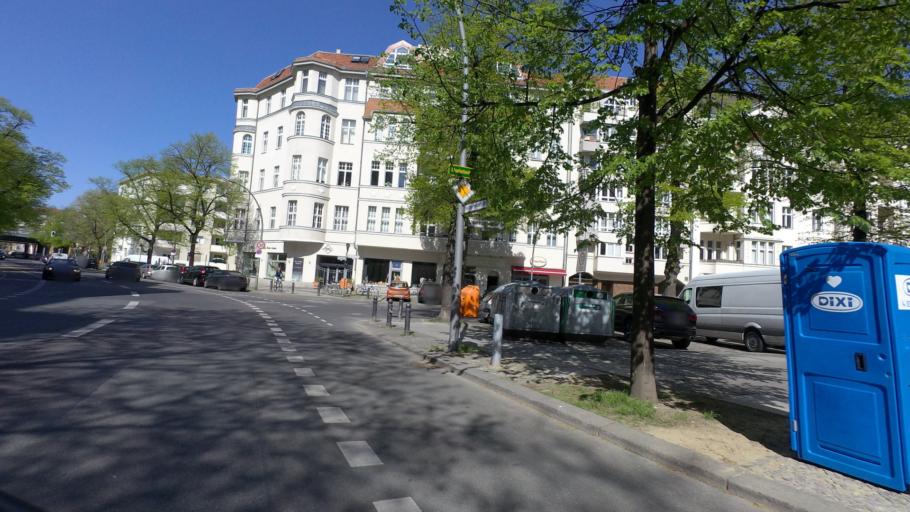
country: DE
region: Berlin
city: Halensee
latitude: 52.5010
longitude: 13.2968
